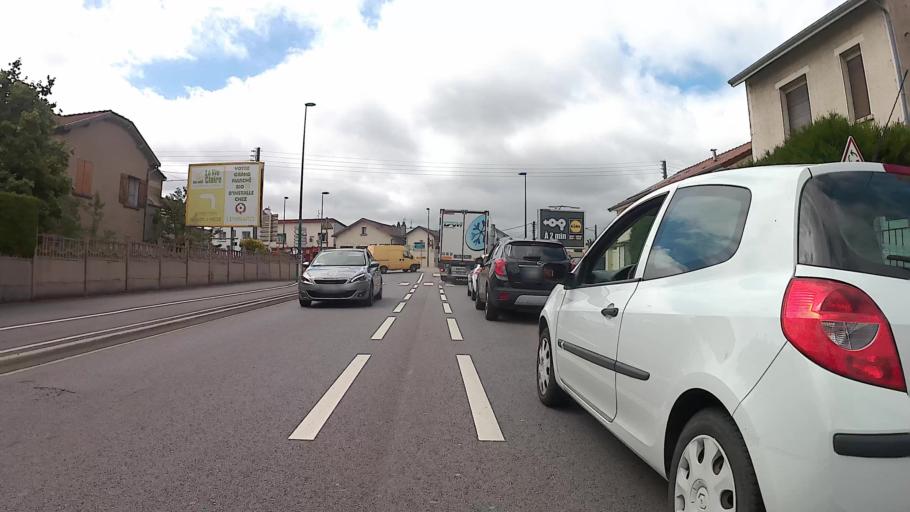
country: FR
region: Lorraine
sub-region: Departement de la Meuse
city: Verdun
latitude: 49.1529
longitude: 5.3963
